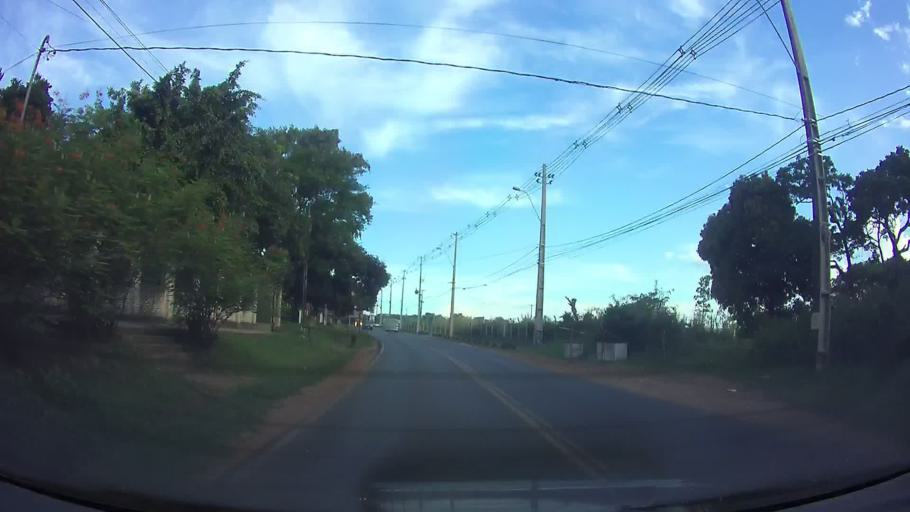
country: PY
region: Central
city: San Antonio
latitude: -25.4286
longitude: -57.5559
